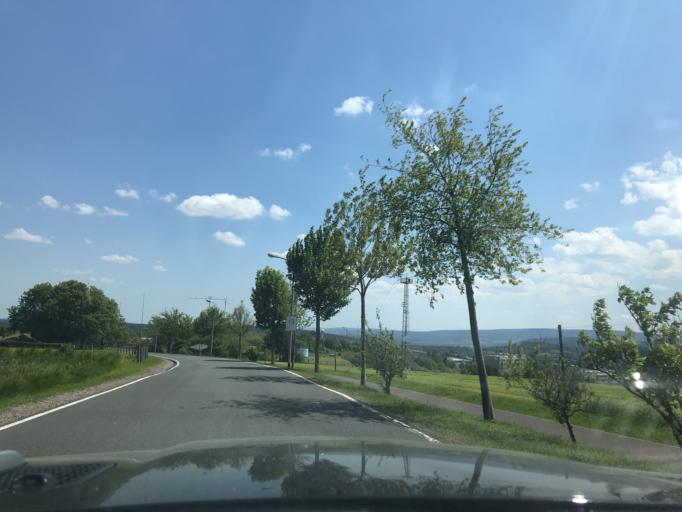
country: DE
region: Thuringia
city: Ilmenau
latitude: 50.7014
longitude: 10.9186
